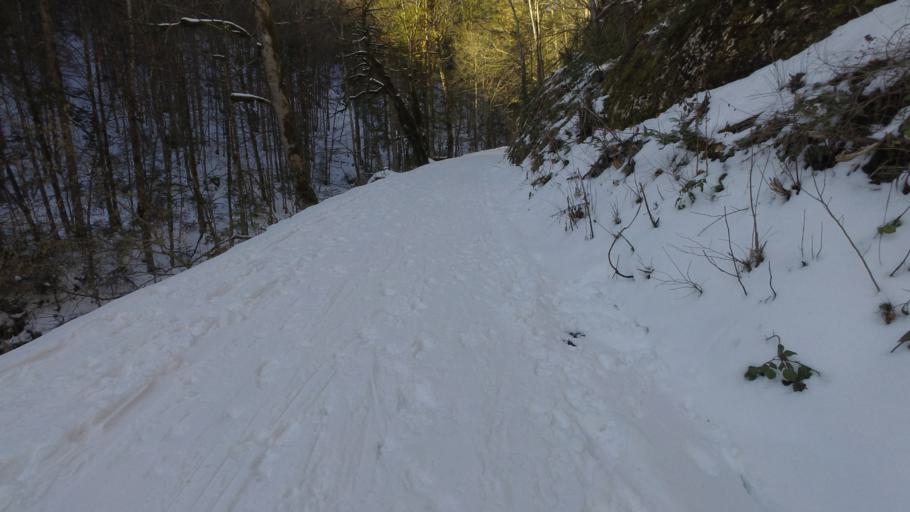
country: DE
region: Bavaria
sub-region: Upper Bavaria
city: Ruhpolding
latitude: 47.7501
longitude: 12.6012
